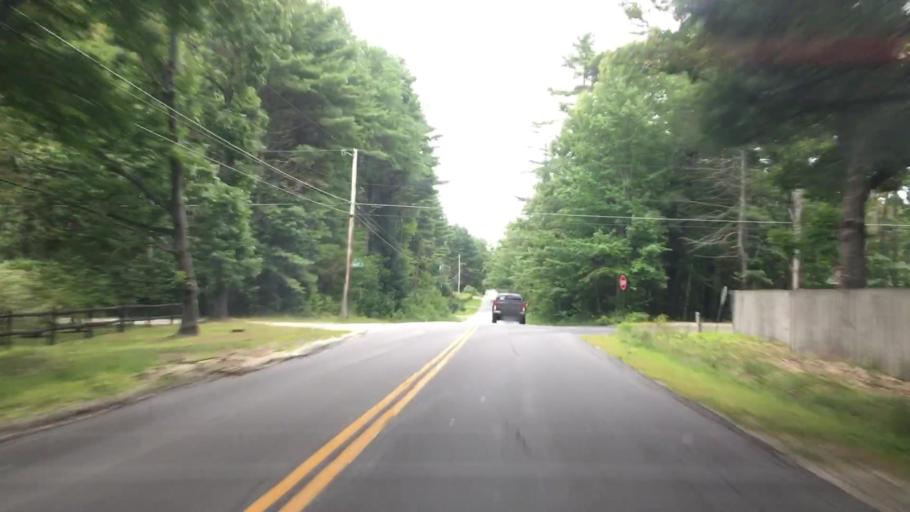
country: US
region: Maine
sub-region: Cumberland County
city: Freeport
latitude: 43.8766
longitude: -70.1523
